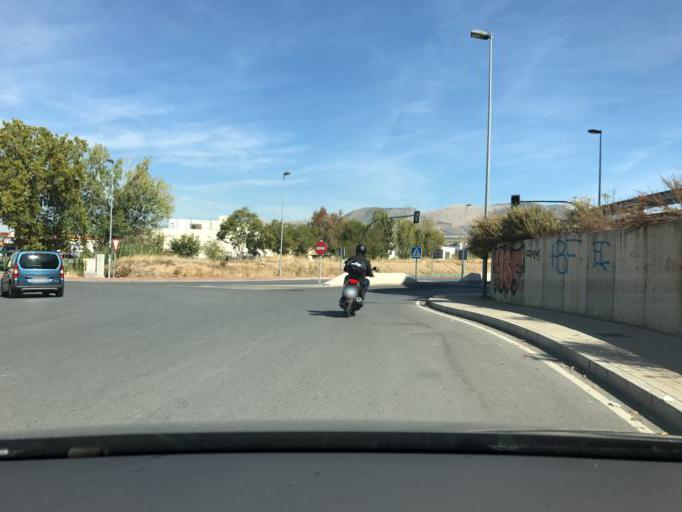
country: ES
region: Andalusia
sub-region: Provincia de Granada
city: Pulianas
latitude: 37.2122
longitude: -3.6100
